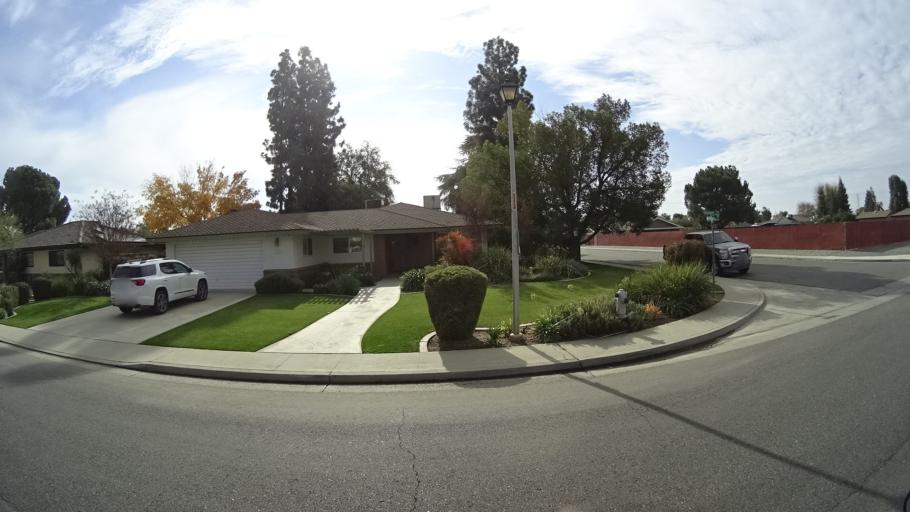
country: US
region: California
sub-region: Kern County
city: Greenacres
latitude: 35.4096
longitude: -119.0875
